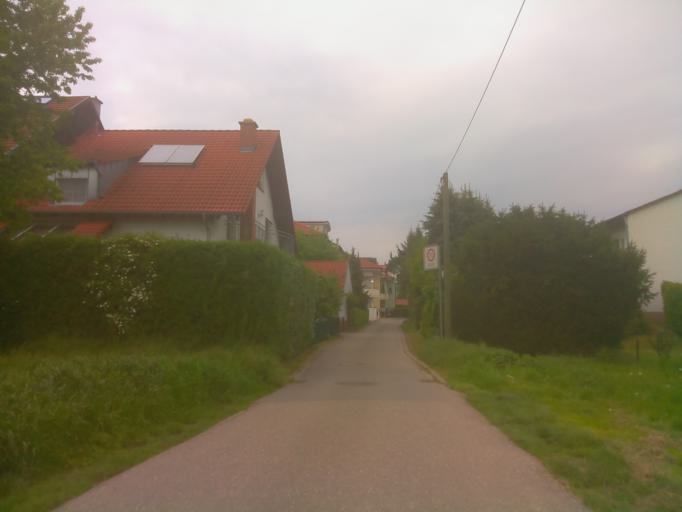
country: DE
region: Baden-Wuerttemberg
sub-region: Karlsruhe Region
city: Schriesheim
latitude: 49.4683
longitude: 8.6548
